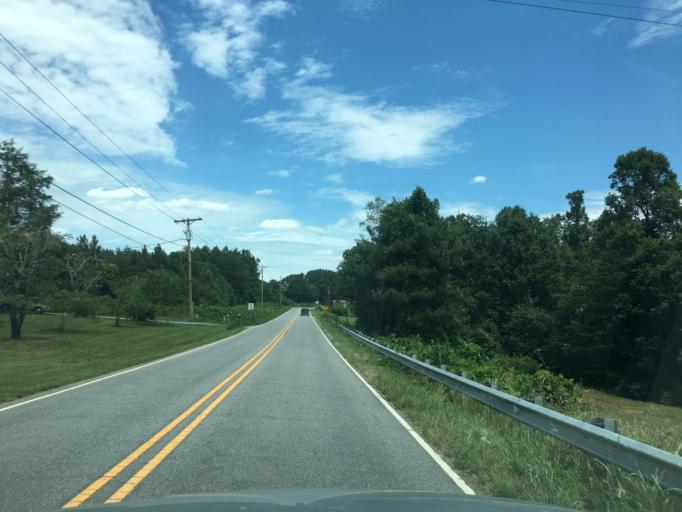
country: US
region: North Carolina
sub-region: Burke County
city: Glen Alpine
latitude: 35.6826
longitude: -81.7696
